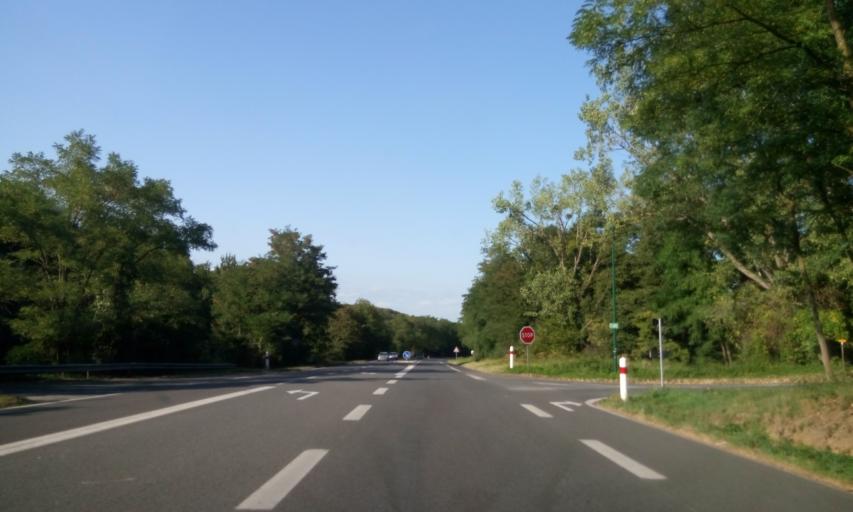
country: FR
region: Rhone-Alpes
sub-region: Departement du Rhone
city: Lissieu
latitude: 45.8516
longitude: 4.7337
